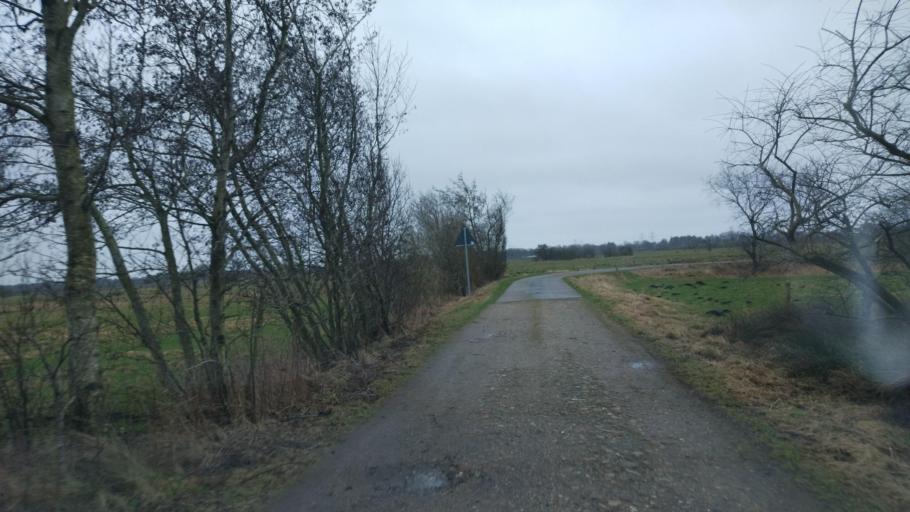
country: DE
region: Schleswig-Holstein
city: Gross Rheide
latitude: 54.4556
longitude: 9.4336
